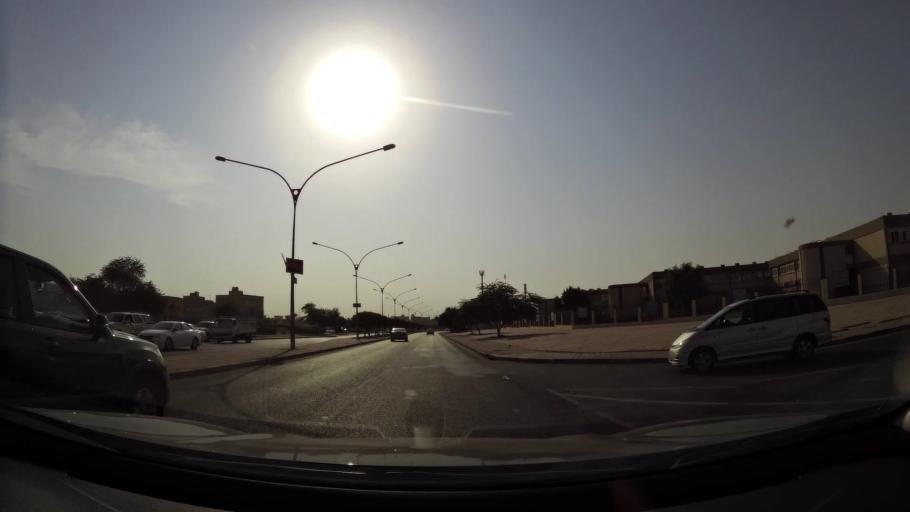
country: KW
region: Mubarak al Kabir
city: Mubarak al Kabir
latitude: 29.1654
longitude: 48.0648
